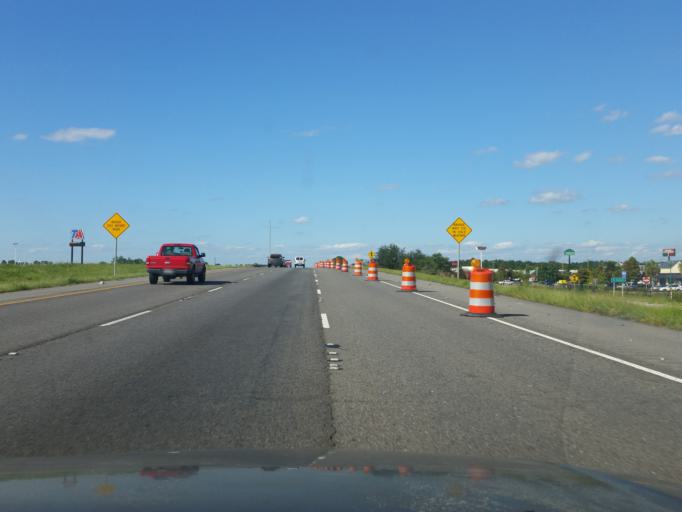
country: US
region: Louisiana
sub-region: Saint Tammany Parish
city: Slidell
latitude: 30.2825
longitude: -89.7503
